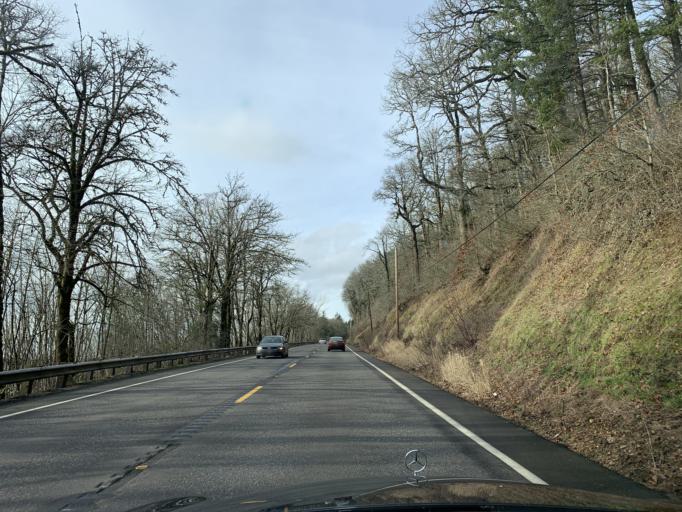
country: US
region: Washington
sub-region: Clark County
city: Washougal
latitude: 45.5625
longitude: -122.2697
